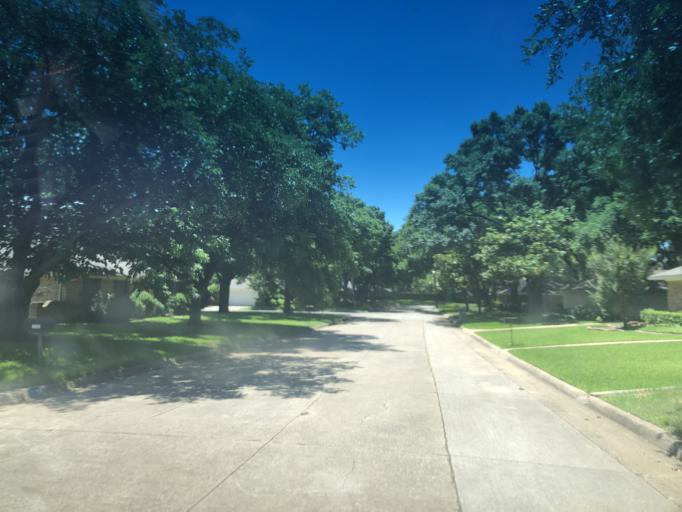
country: US
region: Texas
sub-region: Dallas County
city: Grand Prairie
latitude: 32.7744
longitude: -97.0357
